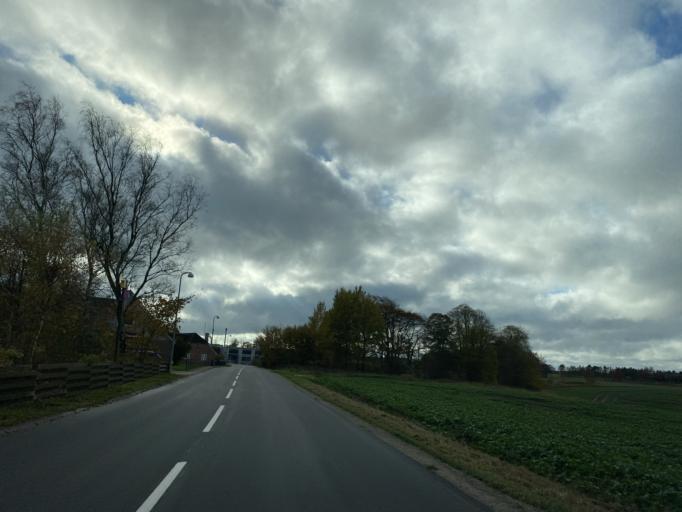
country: DK
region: Central Jutland
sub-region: Favrskov Kommune
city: Hammel
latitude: 56.2448
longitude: 9.8159
